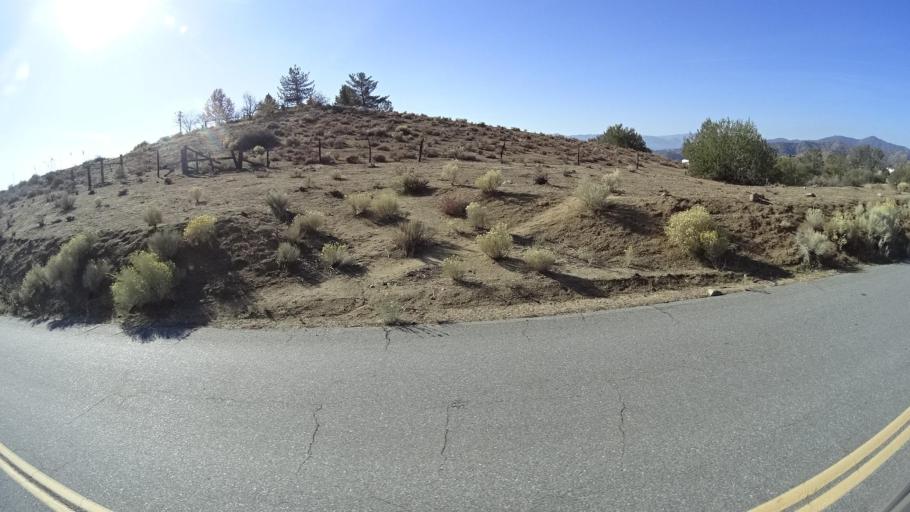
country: US
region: California
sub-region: Kern County
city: Bodfish
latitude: 35.3684
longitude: -118.3904
